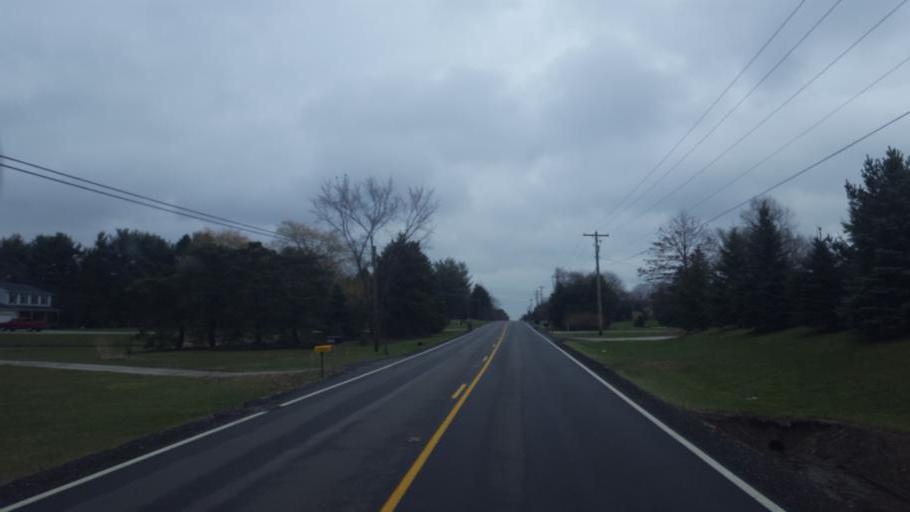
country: US
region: Ohio
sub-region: Medina County
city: Medina
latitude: 41.1067
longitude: -81.8586
